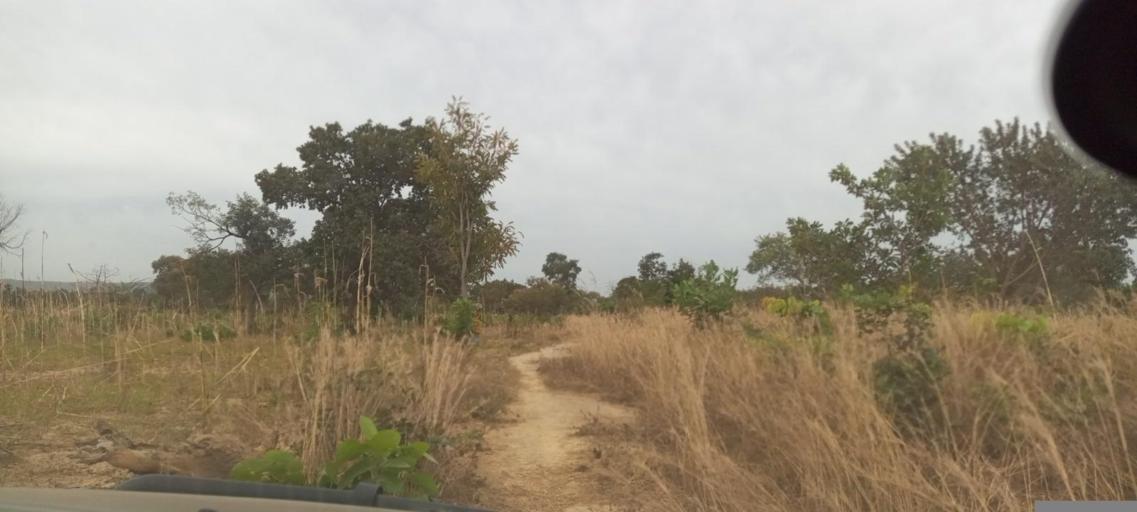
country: ML
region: Koulikoro
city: Kati
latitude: 12.7459
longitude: -8.3509
